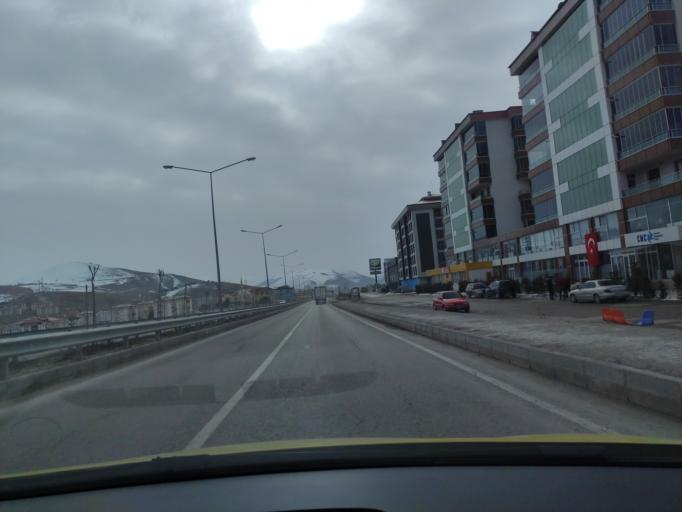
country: TR
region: Bayburt
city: Bayburt
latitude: 40.2682
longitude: 40.1997
